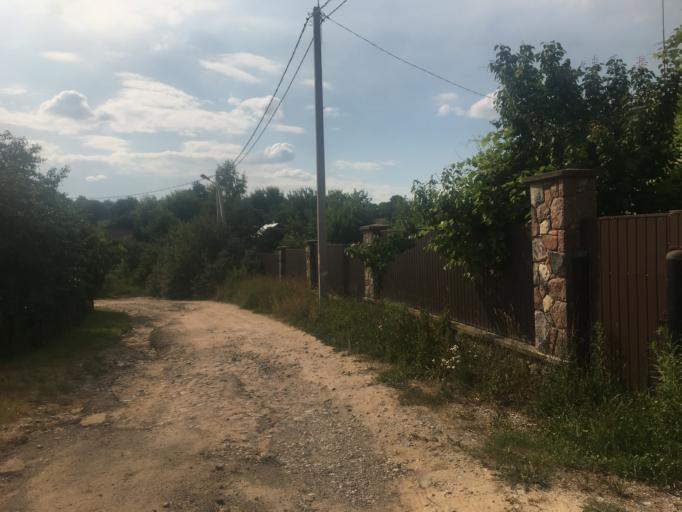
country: BY
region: Grodnenskaya
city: Hrodna
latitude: 53.6827
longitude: 23.8133
